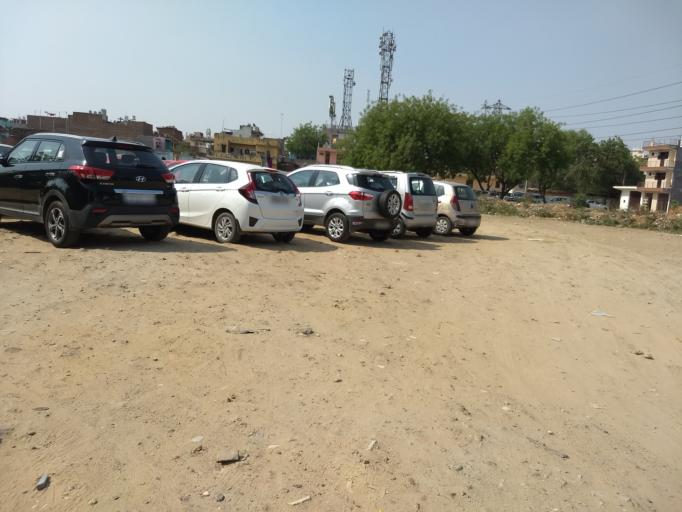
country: IN
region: Haryana
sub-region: Gurgaon
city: Gurgaon
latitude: 28.4477
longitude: 77.0440
